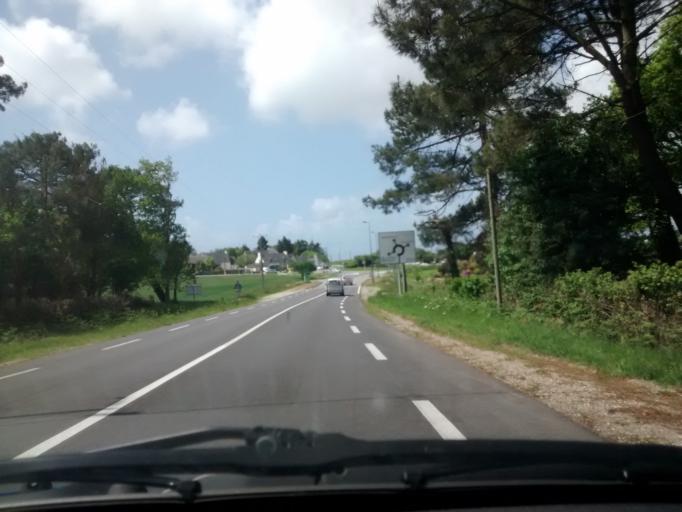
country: FR
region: Brittany
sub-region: Departement du Morbihan
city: Larmor-Baden
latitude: 47.6135
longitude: -2.8833
